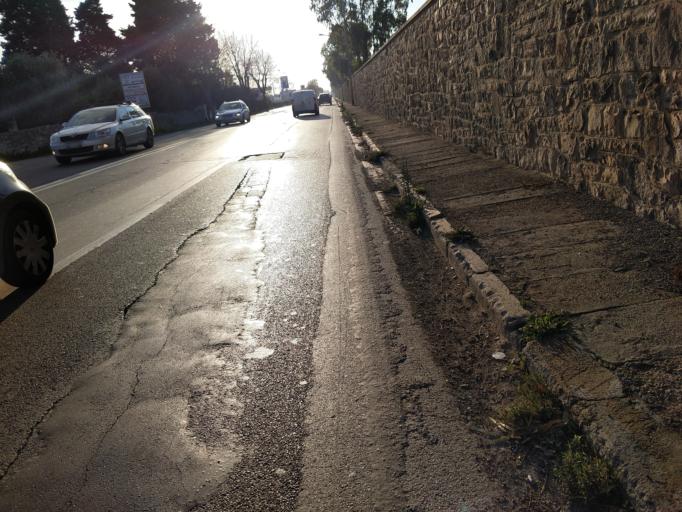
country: IT
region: Apulia
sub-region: Provincia di Bari
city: Bari
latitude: 41.1155
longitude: 16.8350
